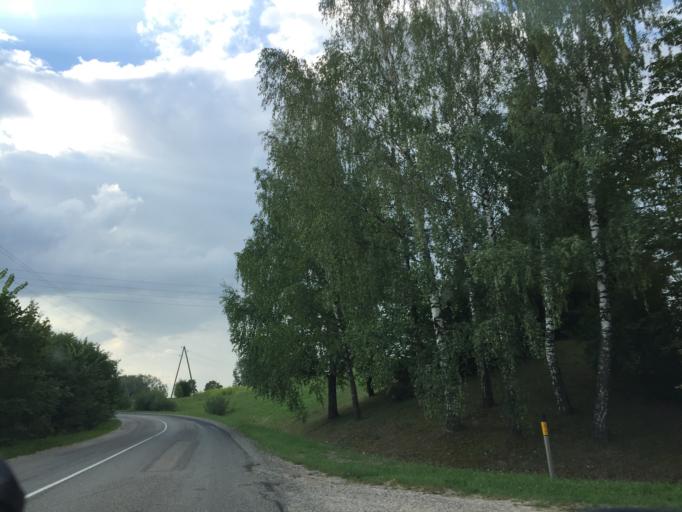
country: LV
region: Dobeles Rajons
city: Dobele
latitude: 56.6012
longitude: 23.3062
